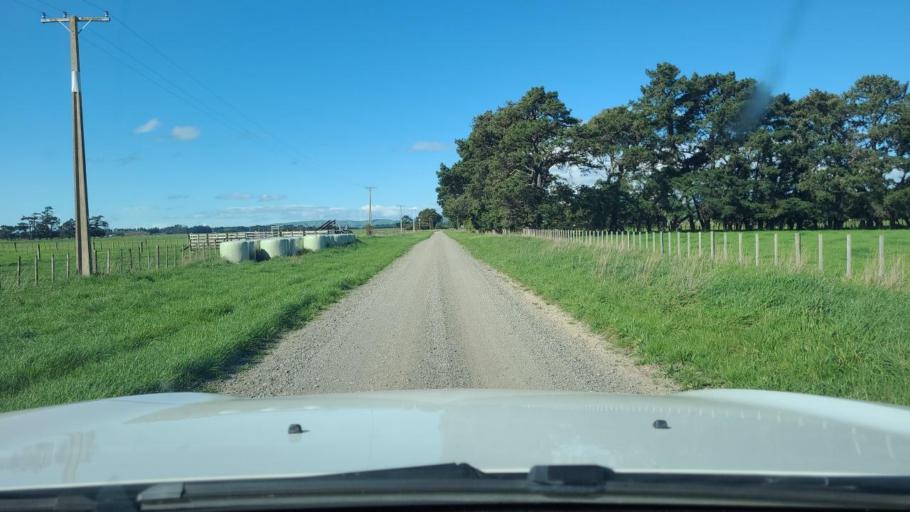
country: NZ
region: Wellington
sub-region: South Wairarapa District
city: Waipawa
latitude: -41.1863
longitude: 175.3638
